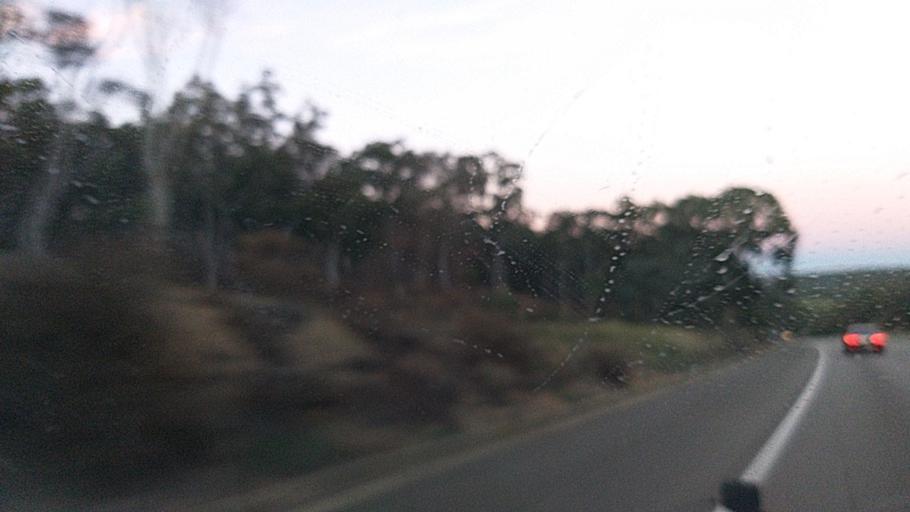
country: AU
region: New South Wales
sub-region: Wingecarribee
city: Bundanoon
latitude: -34.6509
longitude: 150.0927
